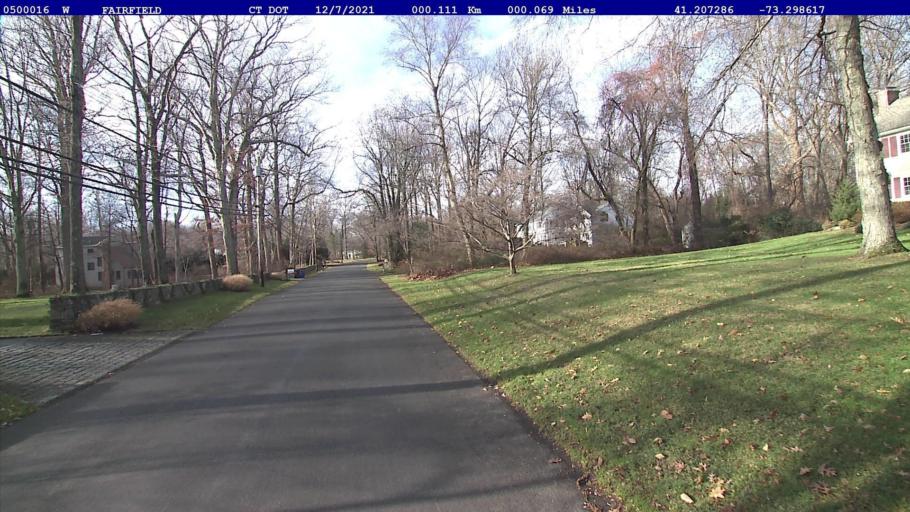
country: US
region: Connecticut
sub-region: Fairfield County
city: Southport
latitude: 41.2075
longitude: -73.2989
